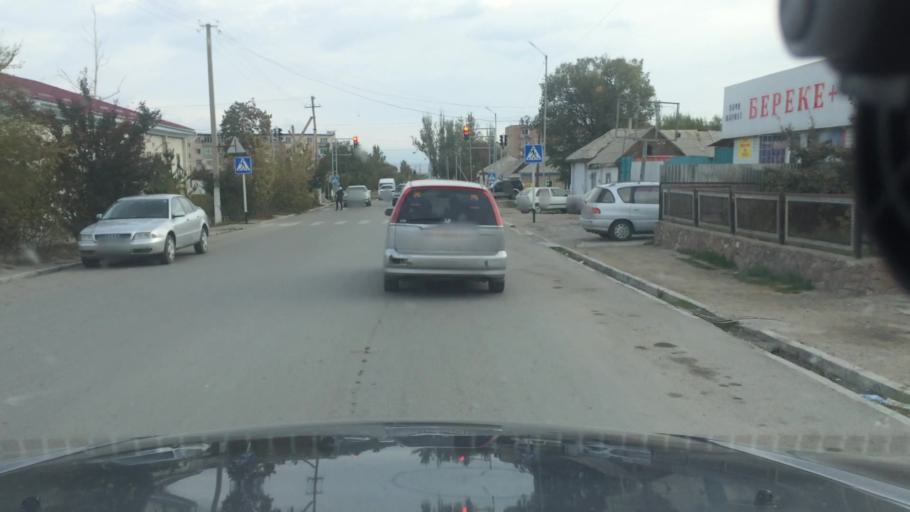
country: KG
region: Ysyk-Koel
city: Karakol
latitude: 42.4942
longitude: 78.3891
